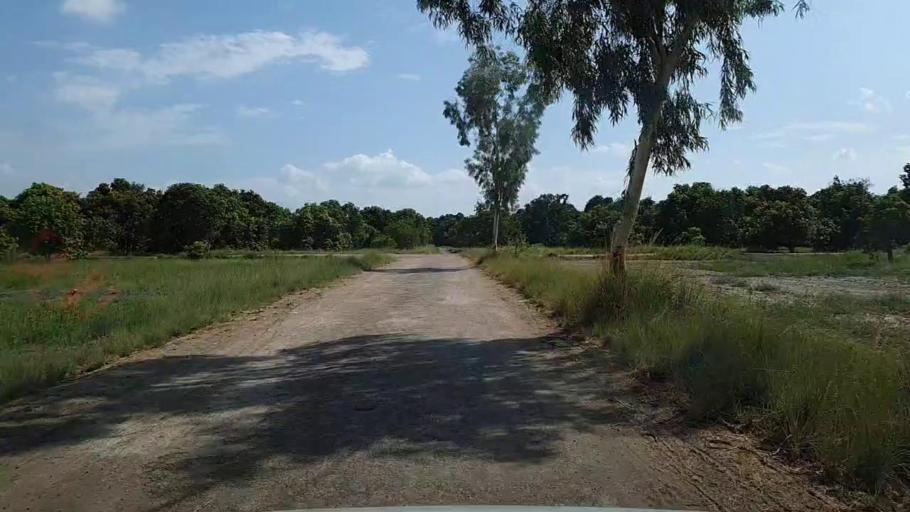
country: PK
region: Sindh
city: Bhiria
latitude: 26.9099
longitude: 68.2249
